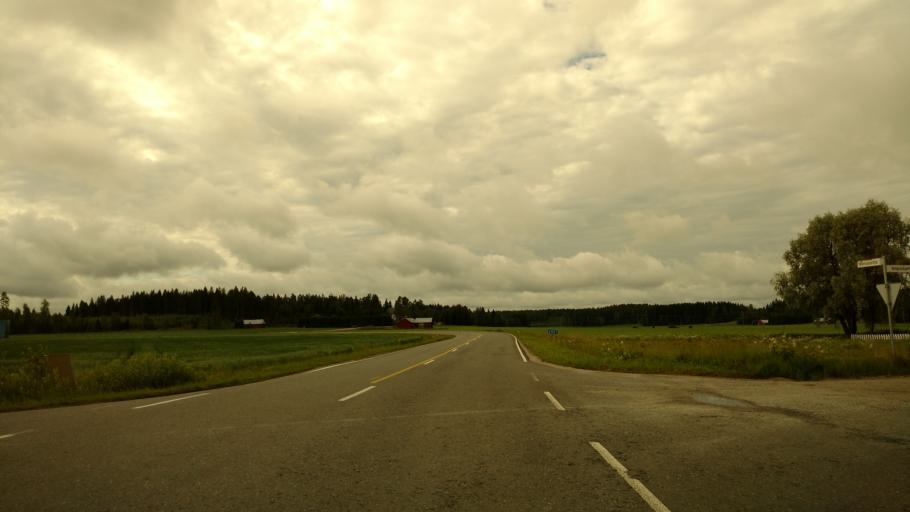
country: FI
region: Varsinais-Suomi
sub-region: Salo
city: Kuusjoki
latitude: 60.5113
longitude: 23.1801
